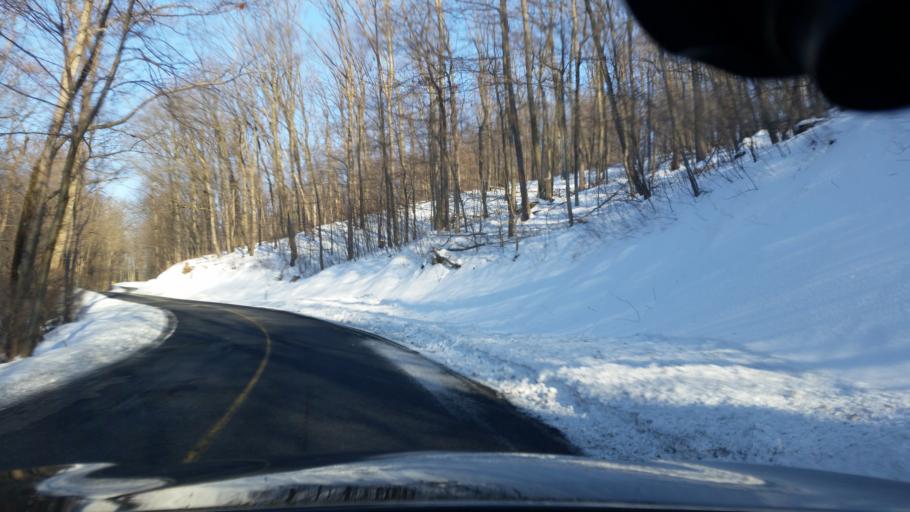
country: US
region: Pennsylvania
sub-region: Perry County
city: Marysville
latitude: 40.3294
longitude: -76.9505
